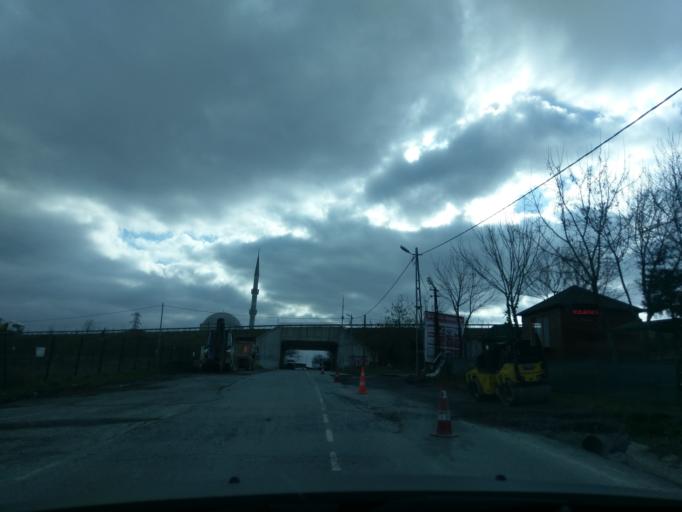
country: TR
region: Istanbul
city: Durusu
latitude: 41.2754
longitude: 28.6610
